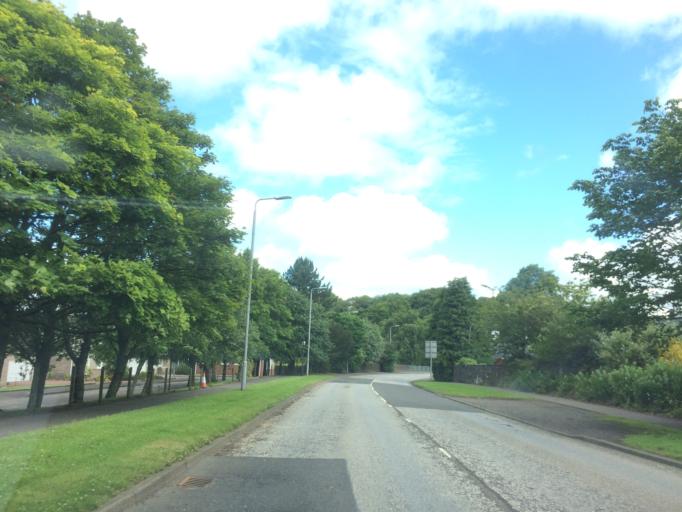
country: GB
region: Scotland
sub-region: East Renfrewshire
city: Newton Mearns
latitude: 55.7775
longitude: -4.3319
